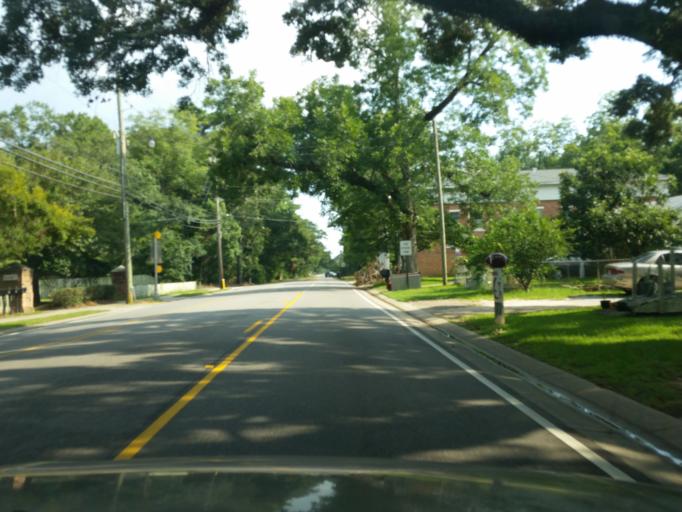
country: US
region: Alabama
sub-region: Baldwin County
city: Daphne
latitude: 30.5986
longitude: -87.9027
